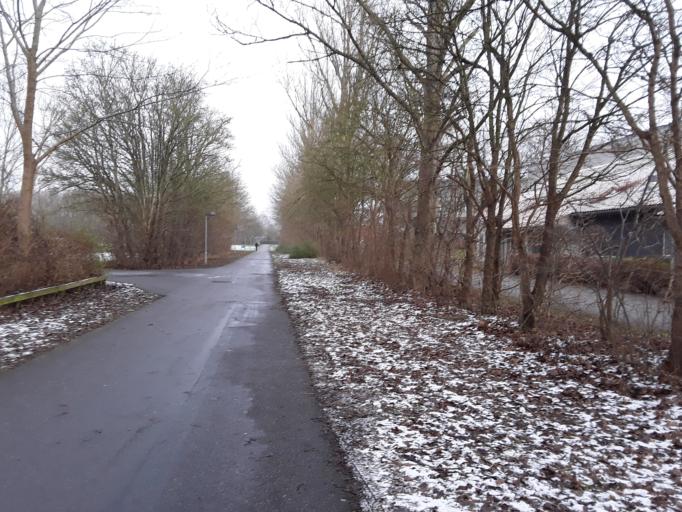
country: DK
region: Zealand
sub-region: Koge Kommune
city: Koge
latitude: 55.4371
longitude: 12.1535
